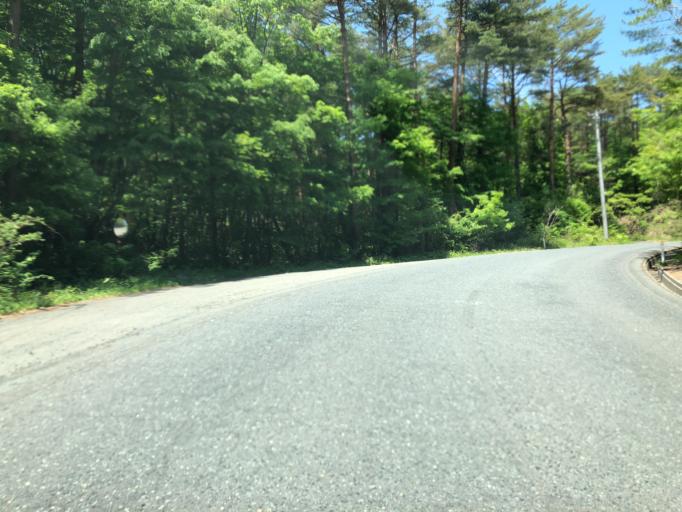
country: JP
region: Fukushima
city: Funehikimachi-funehiki
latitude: 37.5181
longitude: 140.7767
